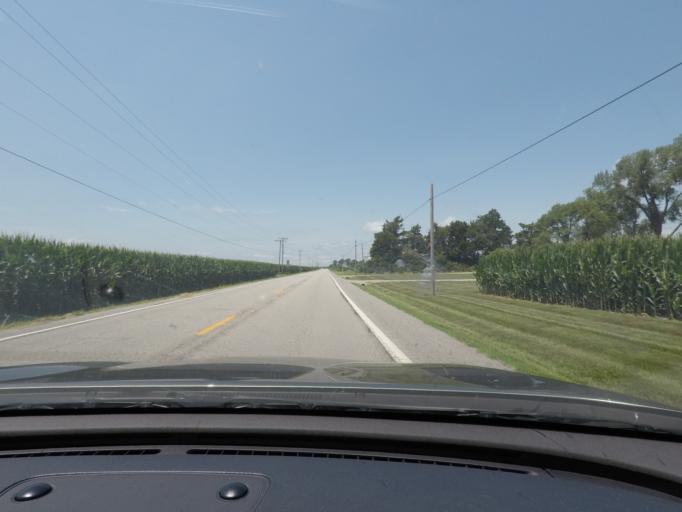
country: US
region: Missouri
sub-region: Saline County
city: Marshall
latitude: 39.1936
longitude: -93.3685
